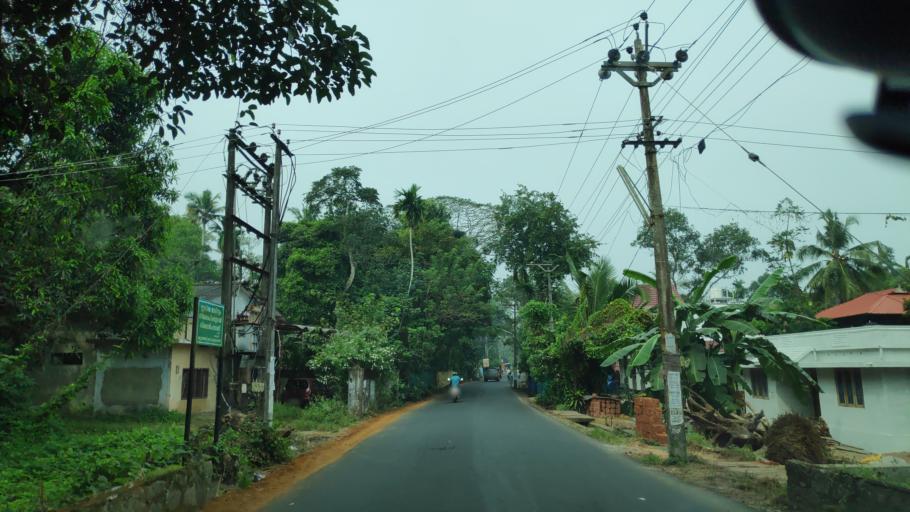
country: IN
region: Kerala
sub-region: Alappuzha
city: Alleppey
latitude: 9.5722
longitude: 76.3451
